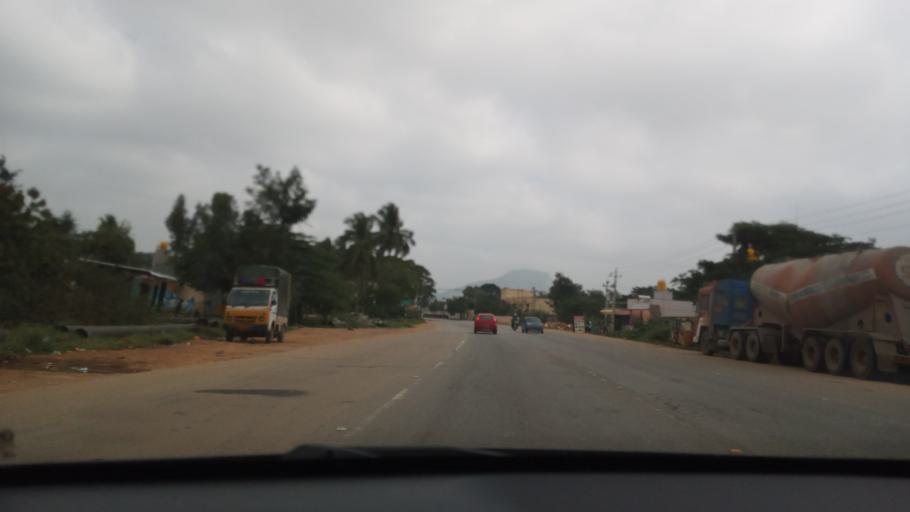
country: IN
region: Karnataka
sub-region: Chikkaballapur
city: Chintamani
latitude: 13.3157
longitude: 77.9806
